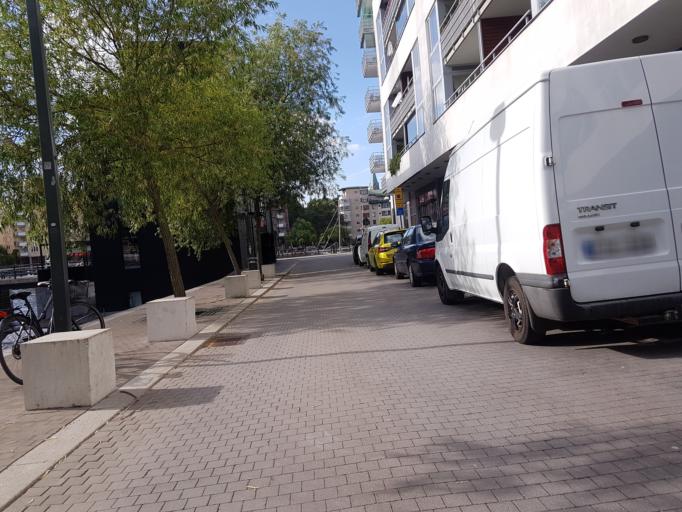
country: SE
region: Stockholm
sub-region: Stockholms Kommun
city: OEstermalm
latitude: 59.3048
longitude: 18.0907
